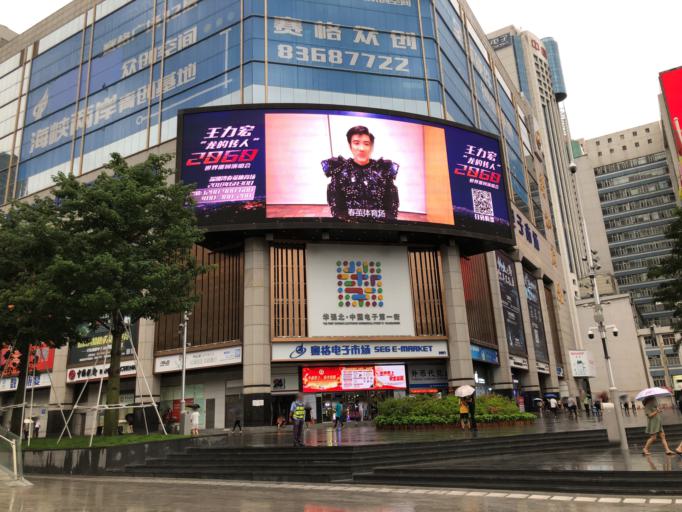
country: CN
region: Guangdong
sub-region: Shenzhen
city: Shenzhen
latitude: 22.5437
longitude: 114.0816
